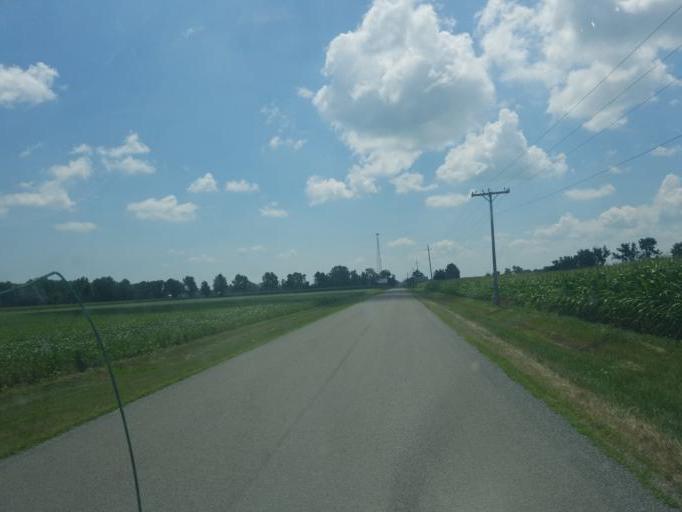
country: US
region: Ohio
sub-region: Mercer County
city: Celina
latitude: 40.5821
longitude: -84.4940
